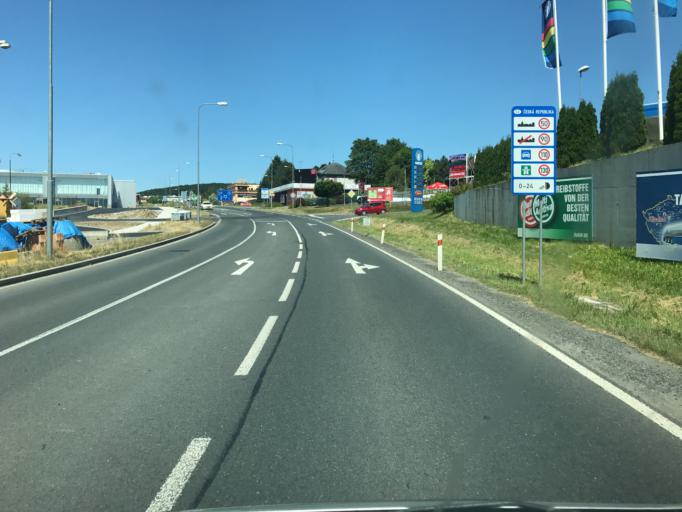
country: DE
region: Bavaria
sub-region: Upper Palatinate
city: Furth im Wald
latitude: 49.3411
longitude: 12.8505
